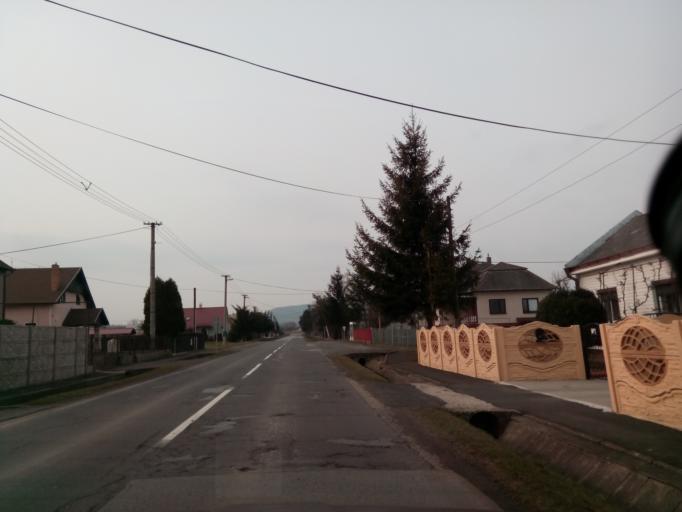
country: SK
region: Kosicky
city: Secovce
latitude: 48.6152
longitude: 21.6020
